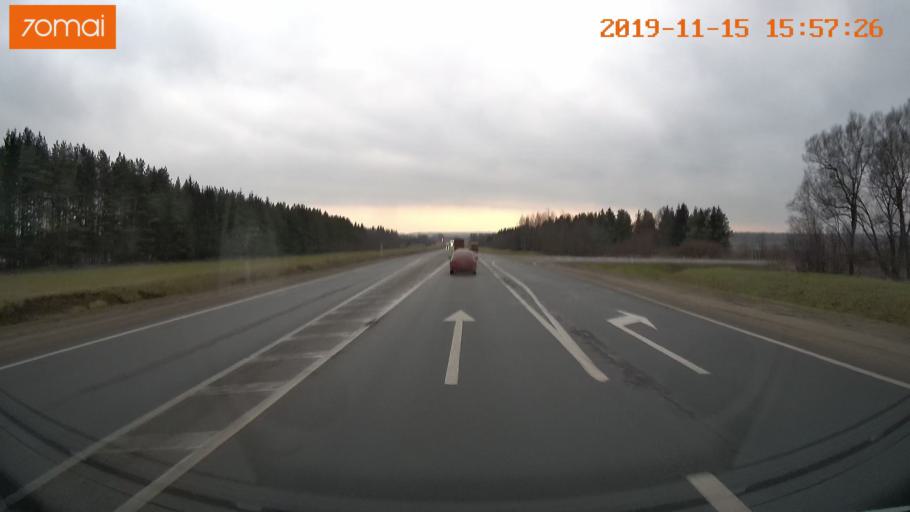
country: RU
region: Jaroslavl
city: Yaroslavl
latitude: 57.8304
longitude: 39.9636
